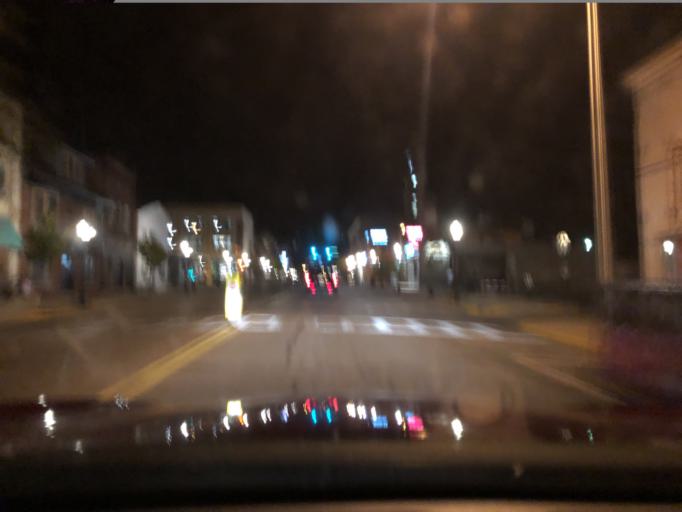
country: US
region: Ohio
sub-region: Logan County
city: Bellefontaine
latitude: 40.3587
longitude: -83.7600
